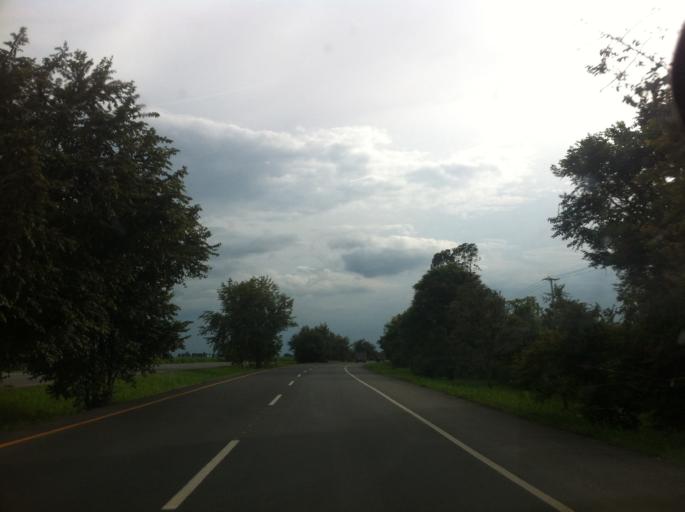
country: CO
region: Valle del Cauca
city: Palmira
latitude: 3.5657
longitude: -76.3335
